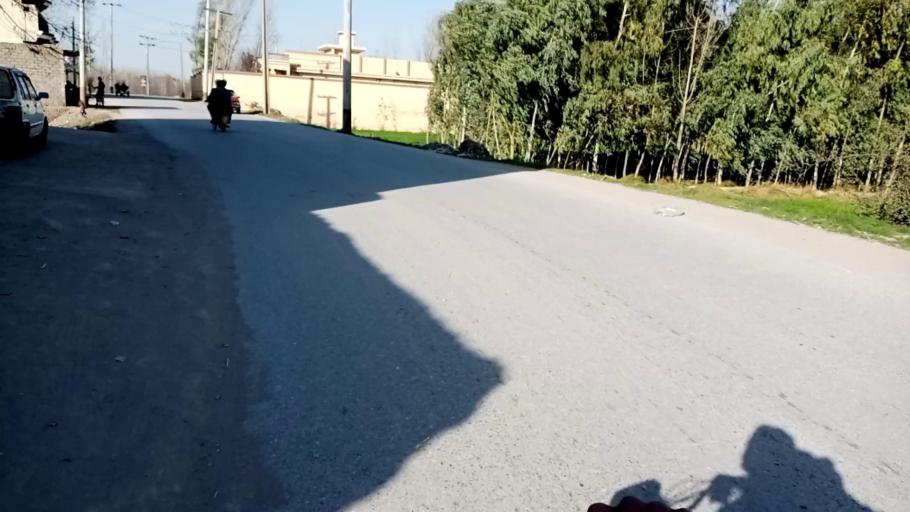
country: PK
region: Khyber Pakhtunkhwa
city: Peshawar
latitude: 34.0498
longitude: 71.5268
